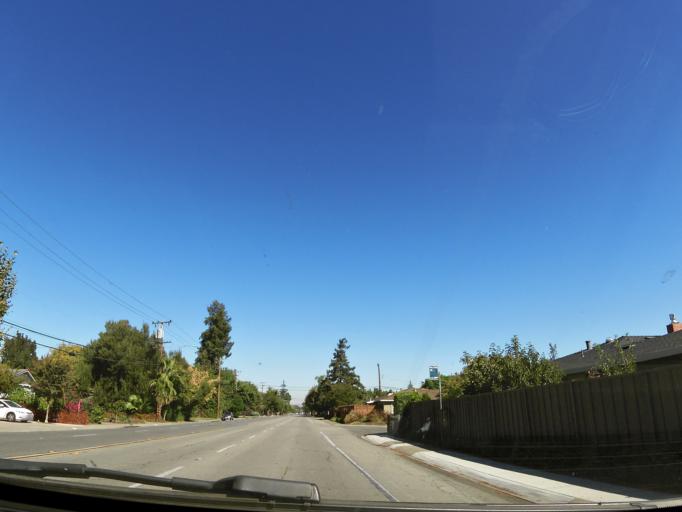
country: US
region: California
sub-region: Santa Clara County
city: Campbell
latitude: 37.2871
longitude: -121.9226
